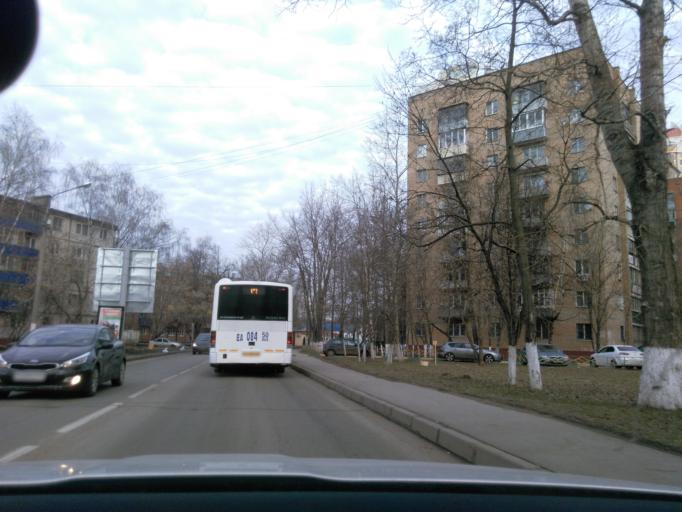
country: RU
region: Moskovskaya
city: Levoberezhnaya
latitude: 55.8942
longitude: 37.4819
